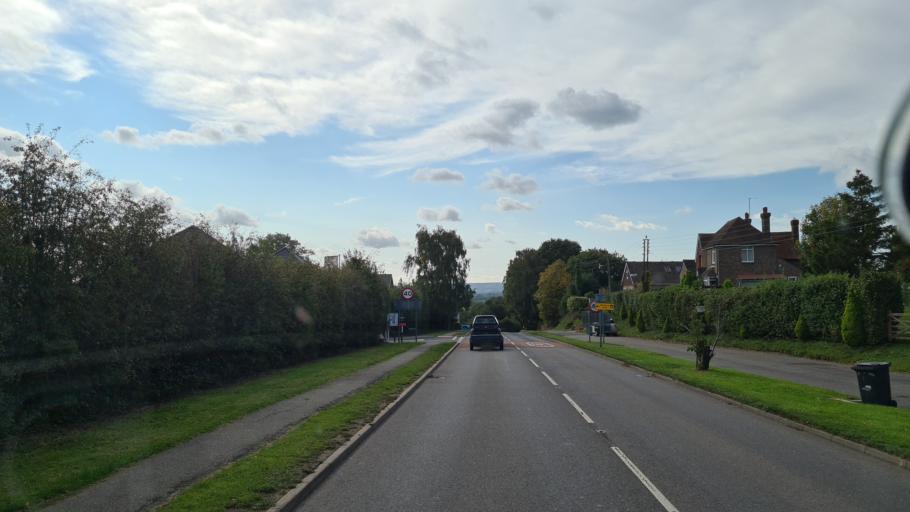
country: GB
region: England
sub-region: East Sussex
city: Bodle Street
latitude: 50.8873
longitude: 0.3174
